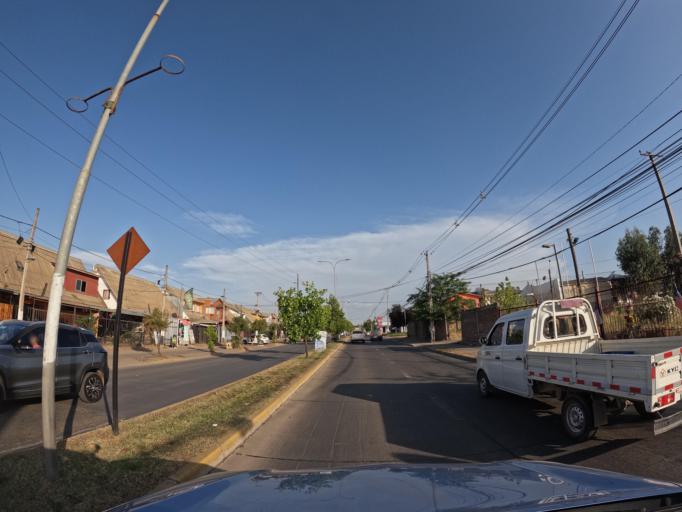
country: CL
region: Maule
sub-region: Provincia de Talca
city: Talca
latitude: -35.4448
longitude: -71.6249
